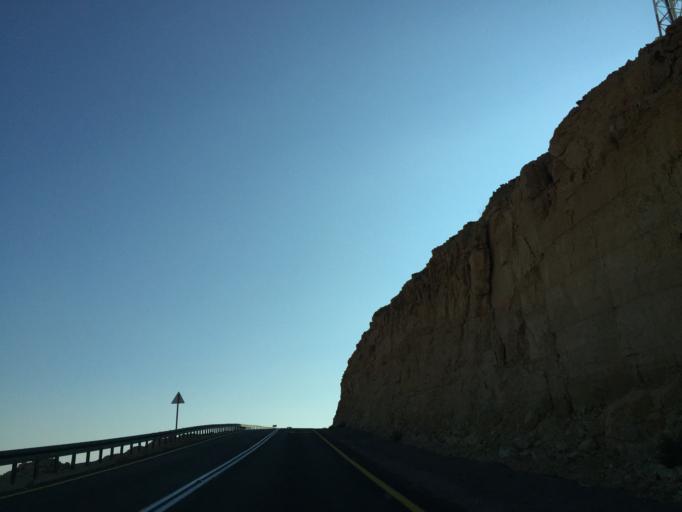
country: JO
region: Ma'an
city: Al Quwayrah
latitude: 30.0211
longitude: 35.0596
